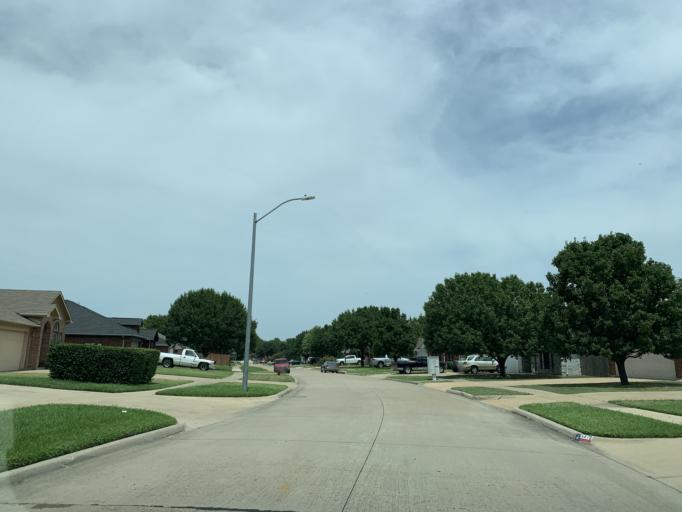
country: US
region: Texas
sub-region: Dallas County
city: Grand Prairie
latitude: 32.6599
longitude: -97.0246
